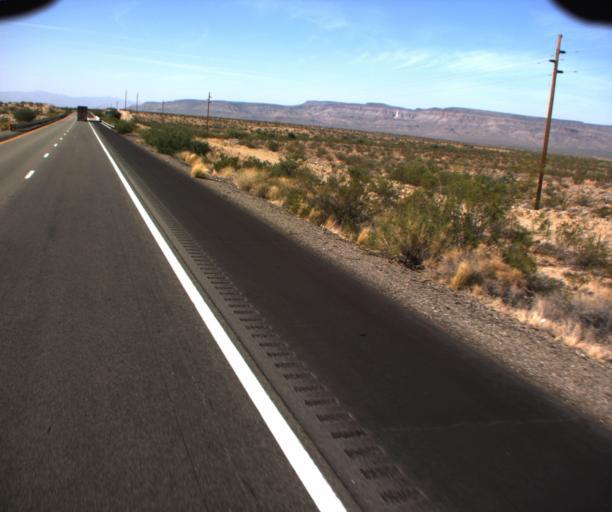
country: US
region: Arizona
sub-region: Mohave County
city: Kingman
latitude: 34.9658
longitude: -114.1435
